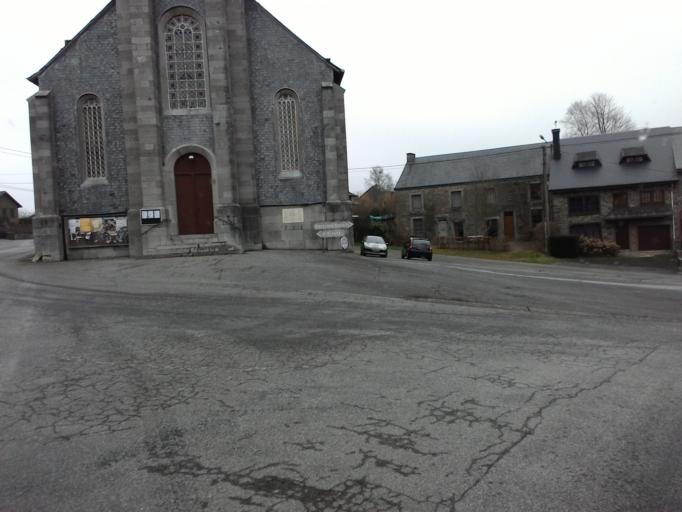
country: BE
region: Wallonia
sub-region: Province de Namur
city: Gedinne
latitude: 50.0224
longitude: 4.8700
